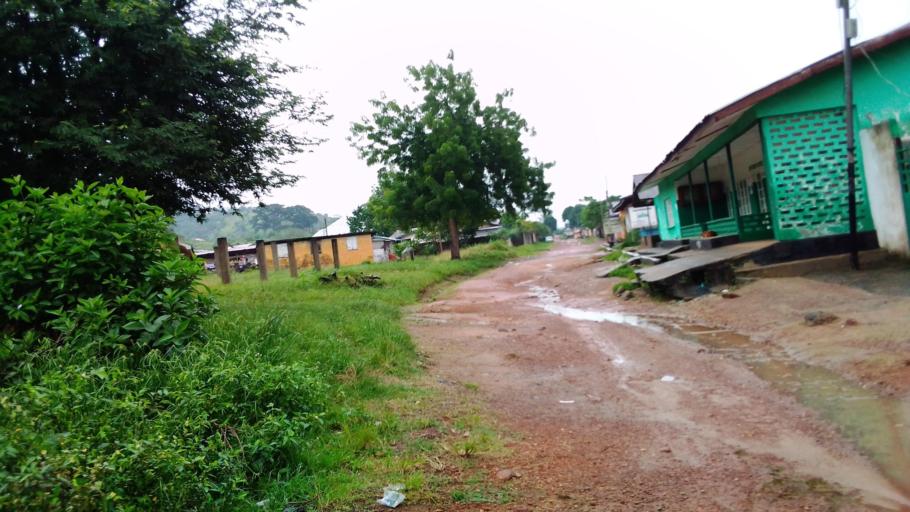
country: SL
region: Eastern Province
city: Kenema
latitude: 7.8886
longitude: -11.1910
